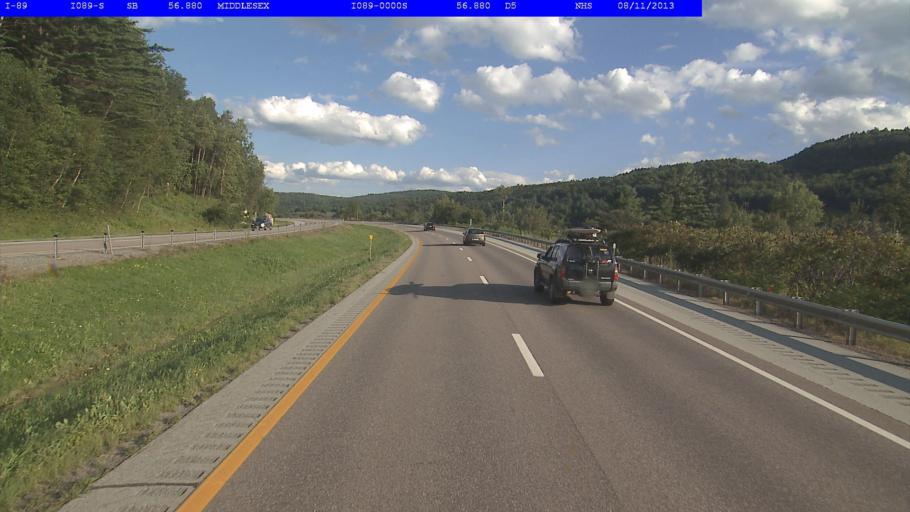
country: US
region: Vermont
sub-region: Washington County
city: Montpelier
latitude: 44.2806
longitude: -72.6593
